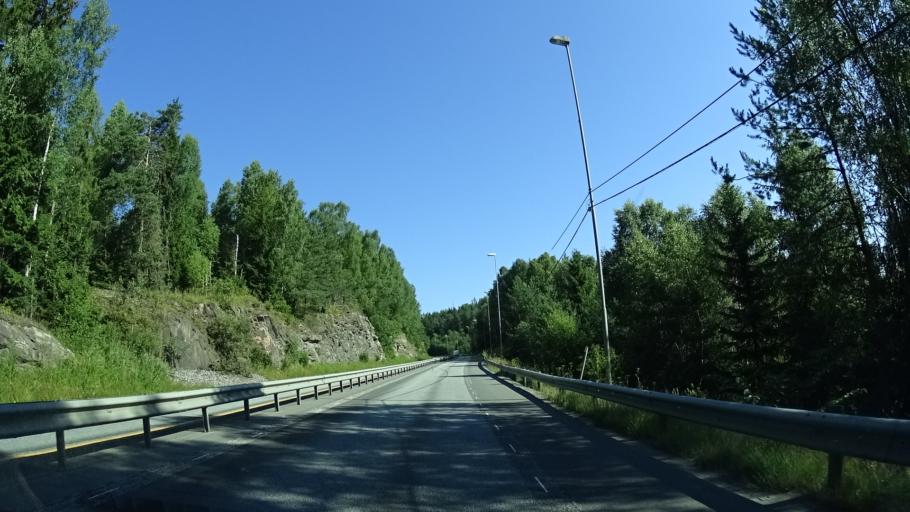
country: NO
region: Akershus
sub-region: Oppegard
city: Kolbotn
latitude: 59.7616
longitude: 10.7751
